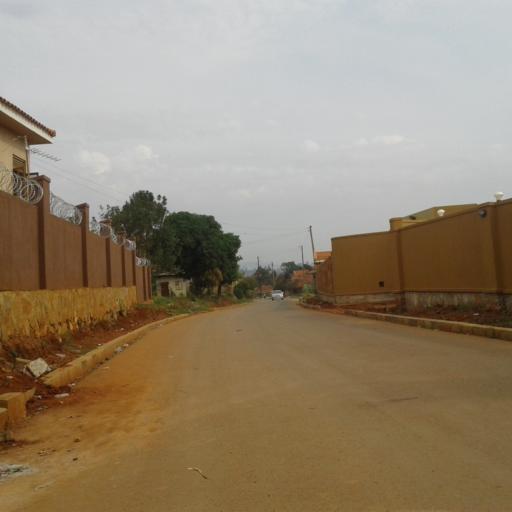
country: UG
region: Central Region
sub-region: Kampala District
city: Kampala
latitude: 0.2726
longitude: 32.6268
